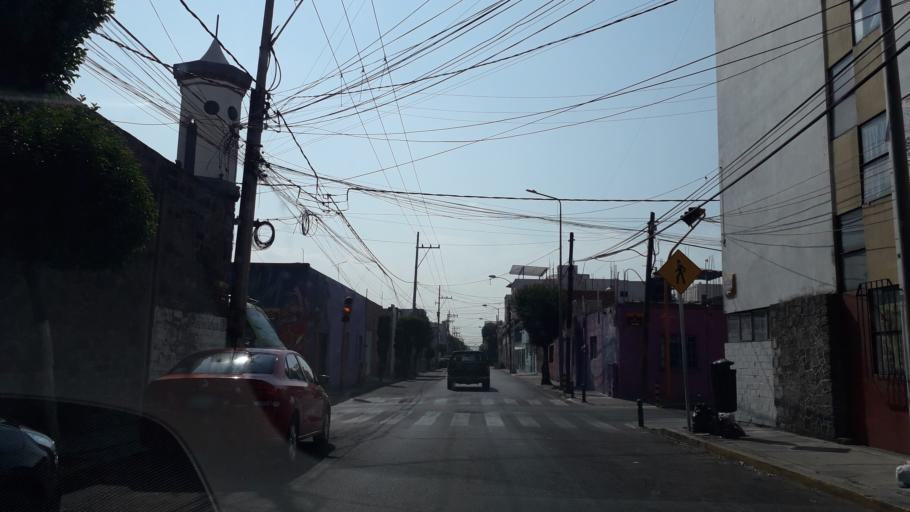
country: MX
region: Puebla
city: Puebla
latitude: 19.0421
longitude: -98.2135
